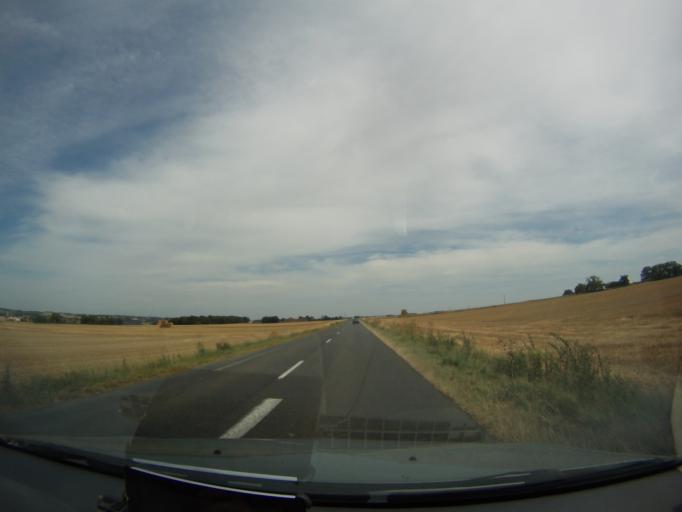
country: FR
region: Poitou-Charentes
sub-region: Departement de la Vienne
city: Saint-Jean-de-Sauves
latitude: 46.7920
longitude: 0.1161
